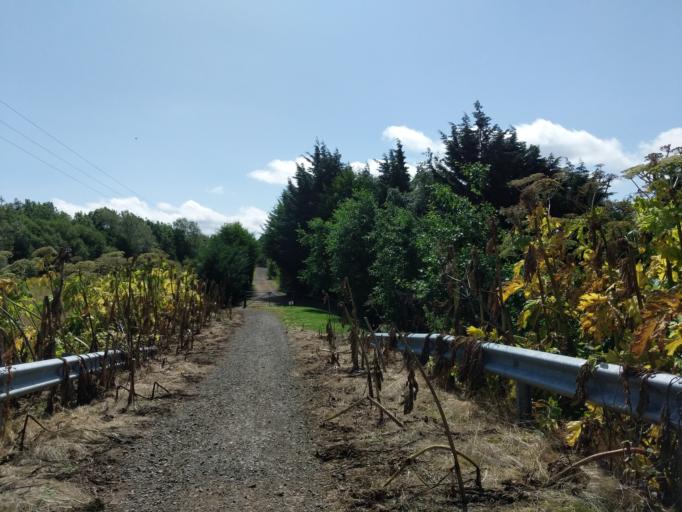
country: GB
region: Scotland
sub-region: Edinburgh
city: Currie
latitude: 55.9264
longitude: -3.3165
